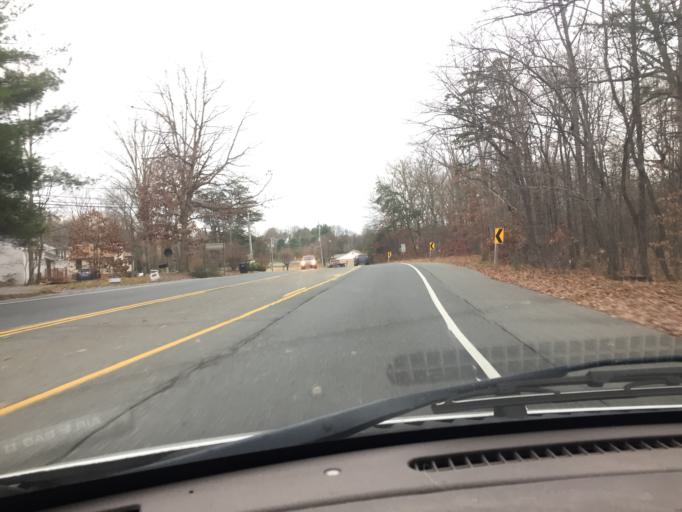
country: US
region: Virginia
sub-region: Bedford County
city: Forest
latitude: 37.3517
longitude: -79.2814
